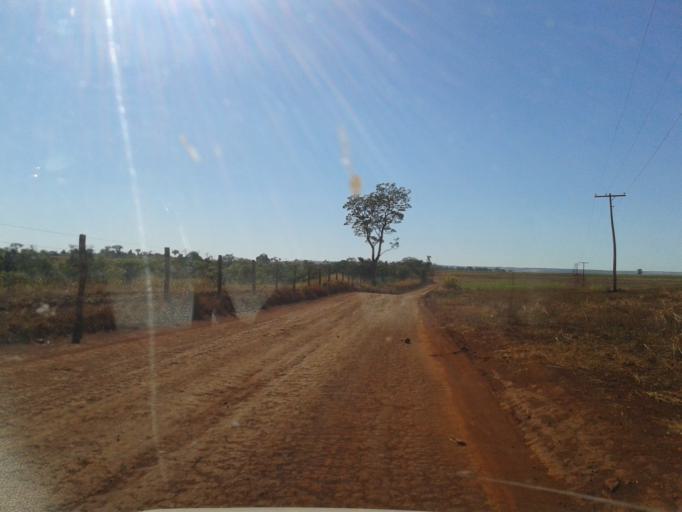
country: BR
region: Minas Gerais
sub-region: Centralina
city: Centralina
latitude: -18.5915
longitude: -49.1696
